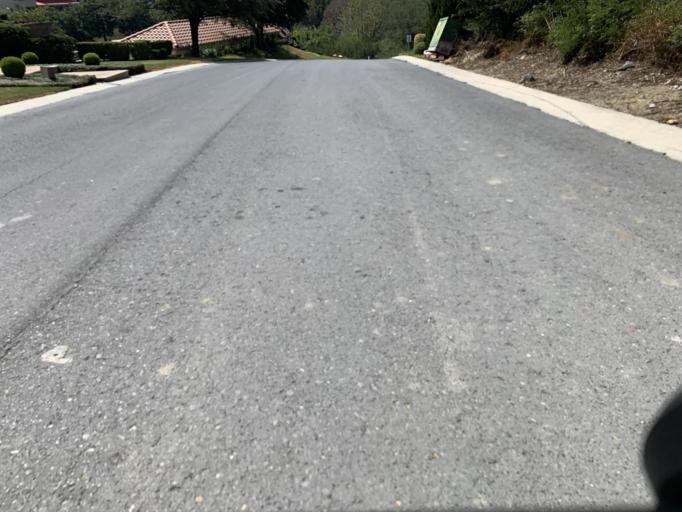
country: MX
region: Nuevo Leon
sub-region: Juarez
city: Bosques de San Pedro
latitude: 25.5212
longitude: -100.1911
